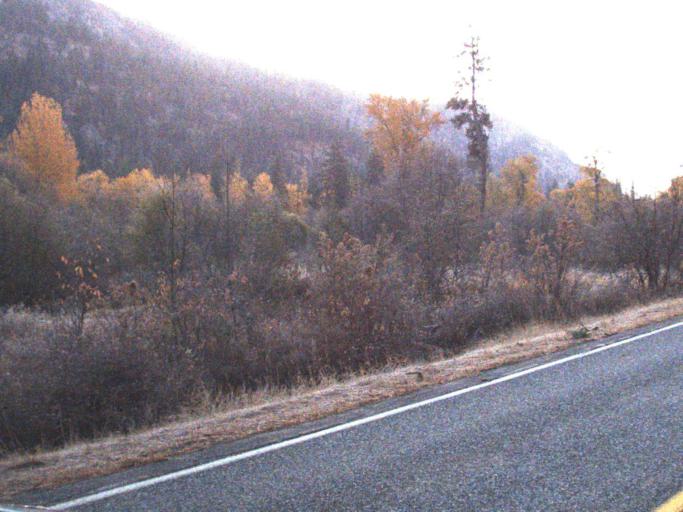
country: US
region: Washington
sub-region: Ferry County
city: Republic
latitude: 48.2948
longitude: -118.7333
